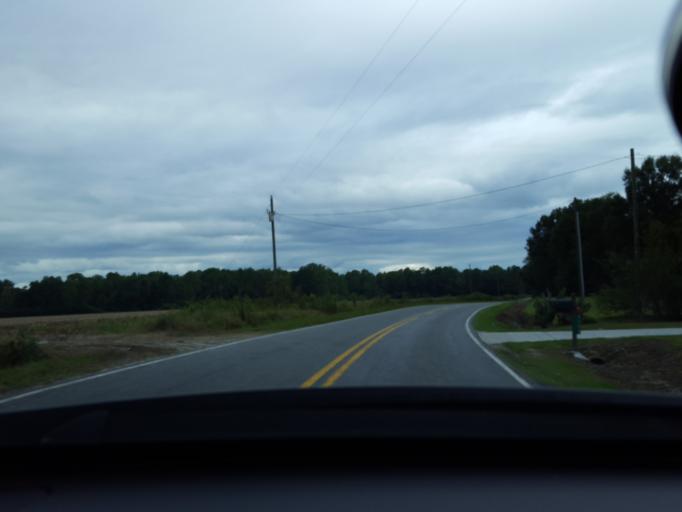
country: US
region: North Carolina
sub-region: Sampson County
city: Clinton
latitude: 34.7834
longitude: -78.3673
